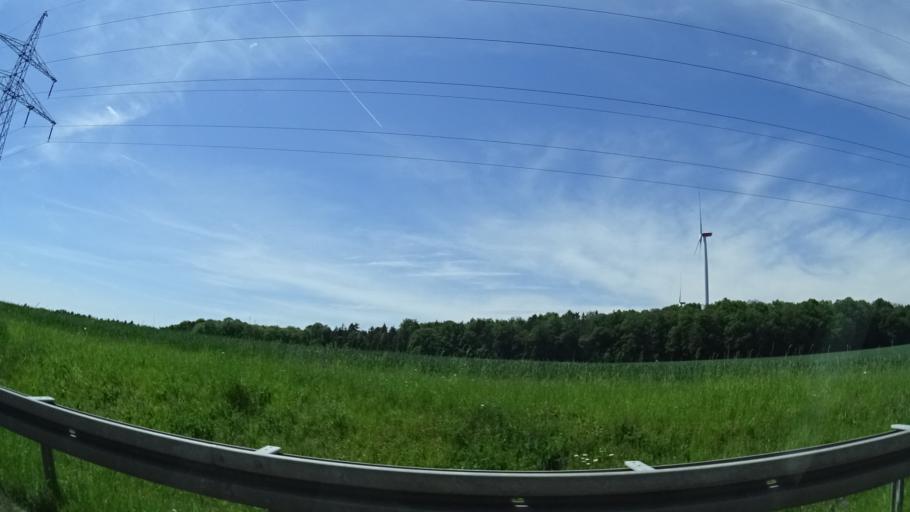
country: DE
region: Bavaria
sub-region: Regierungsbezirk Unterfranken
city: Nudlingen
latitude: 50.2128
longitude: 10.1619
